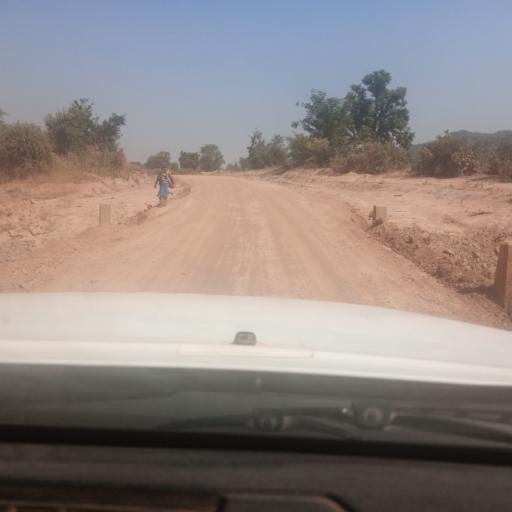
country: NG
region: Adamawa
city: Yola
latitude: 9.0940
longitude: 12.3896
